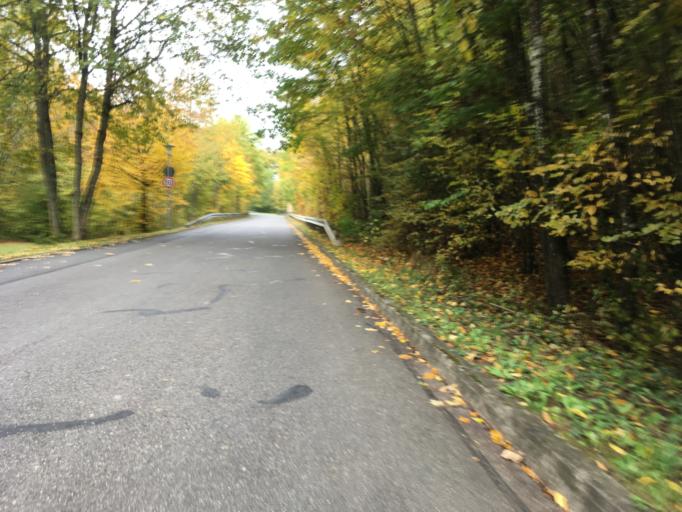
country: DE
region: Baden-Wuerttemberg
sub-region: Karlsruhe Region
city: Seckach
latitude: 49.4407
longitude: 9.3571
